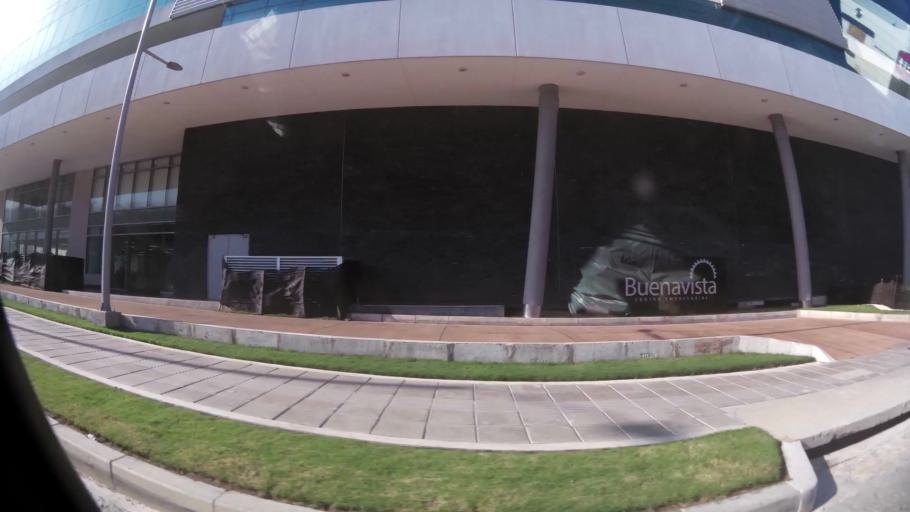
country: CO
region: Atlantico
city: Barranquilla
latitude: 11.0200
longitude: -74.8359
